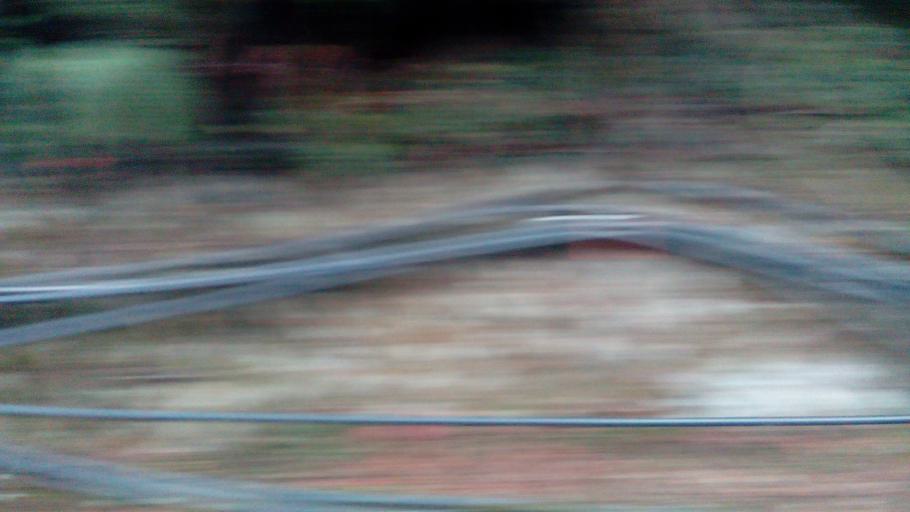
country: TW
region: Taiwan
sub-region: Nantou
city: Puli
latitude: 24.2558
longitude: 121.2505
